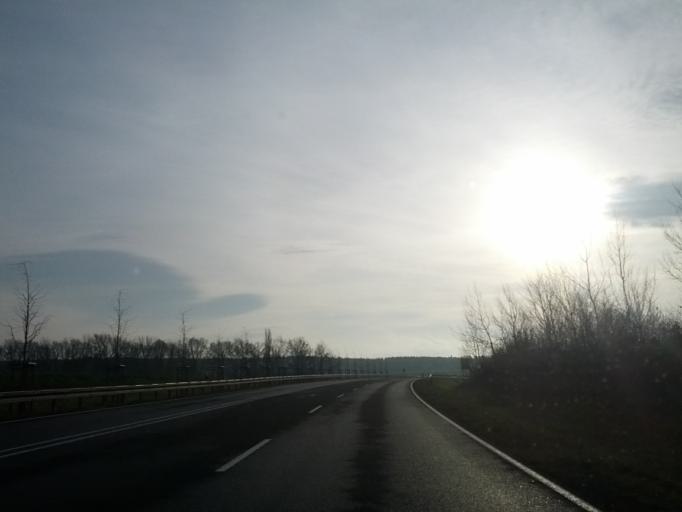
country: DE
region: Thuringia
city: Barchfeld
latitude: 50.8042
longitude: 10.3200
